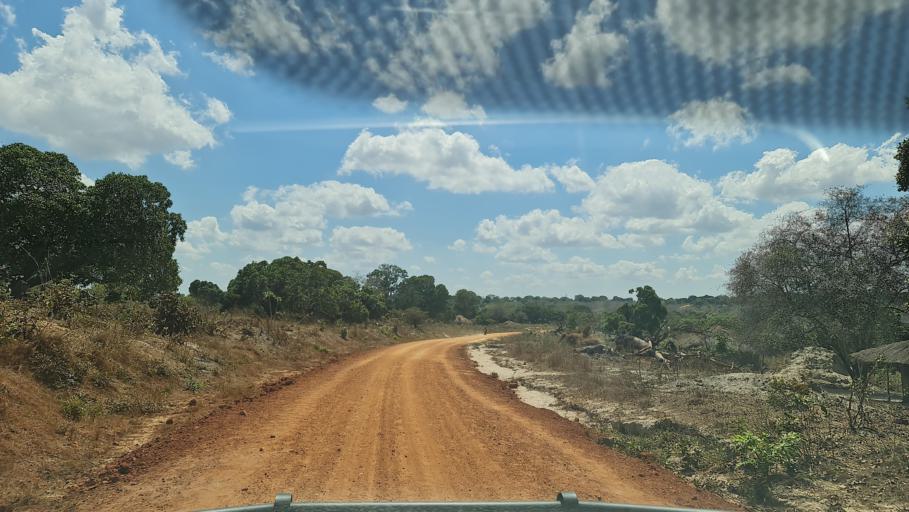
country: MZ
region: Nampula
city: Nacala
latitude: -14.1696
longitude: 40.2476
